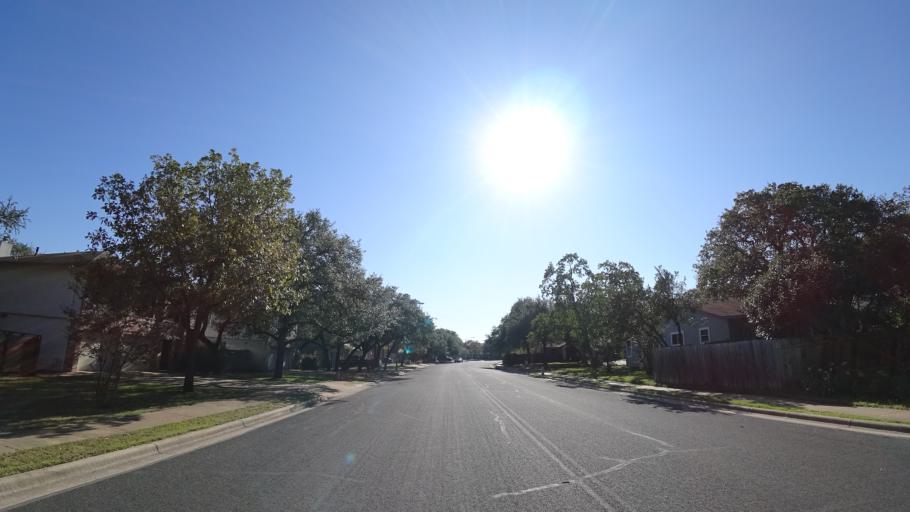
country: US
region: Texas
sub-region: Travis County
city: Shady Hollow
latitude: 30.2069
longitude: -97.8506
